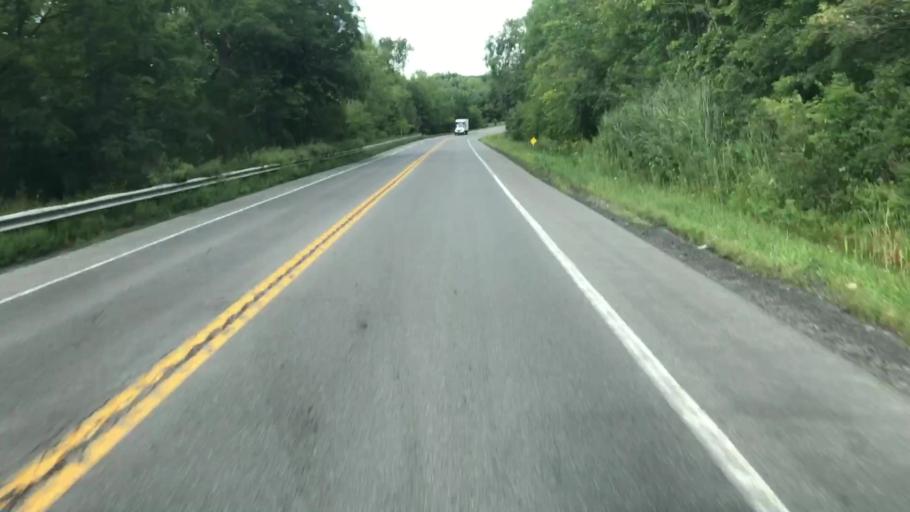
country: US
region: New York
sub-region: Onondaga County
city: Marcellus
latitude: 42.9681
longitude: -76.3368
